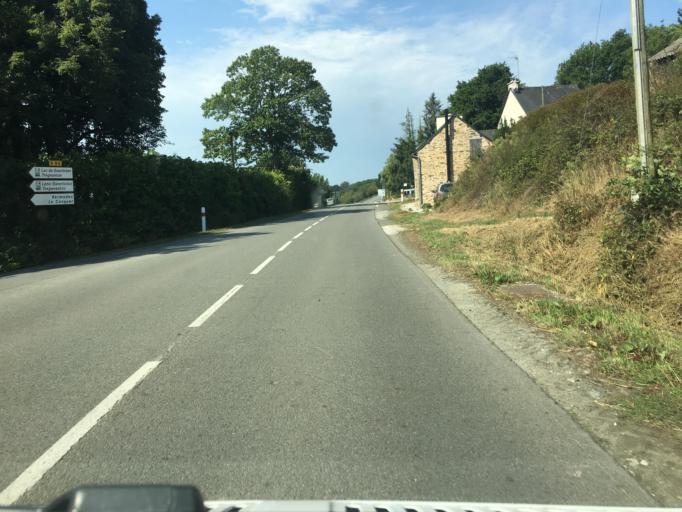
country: FR
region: Brittany
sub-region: Departement des Cotes-d'Armor
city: Gouarec
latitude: 48.2189
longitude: -3.0880
